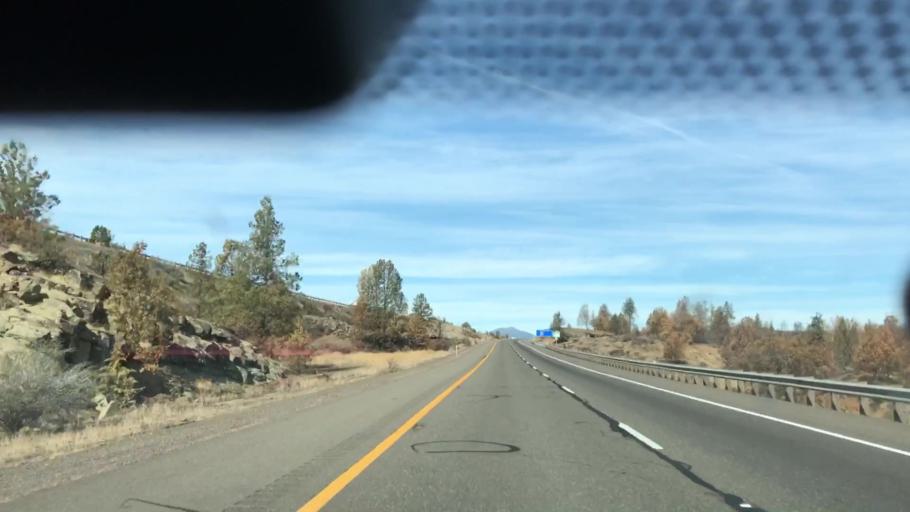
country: US
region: California
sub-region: Siskiyou County
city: Montague
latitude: 41.8880
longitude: -122.5581
